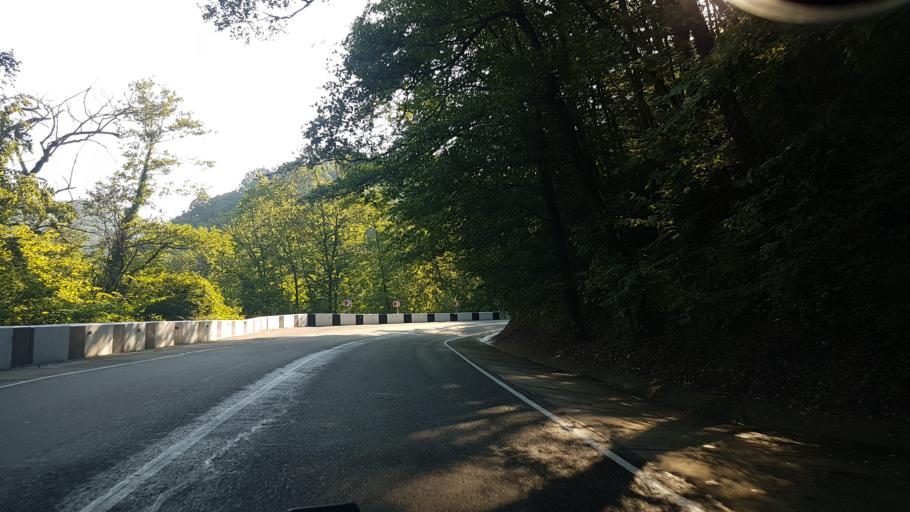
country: RU
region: Krasnodarskiy
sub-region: Sochi City
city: Lazarevskoye
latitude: 43.8736
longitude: 39.3976
